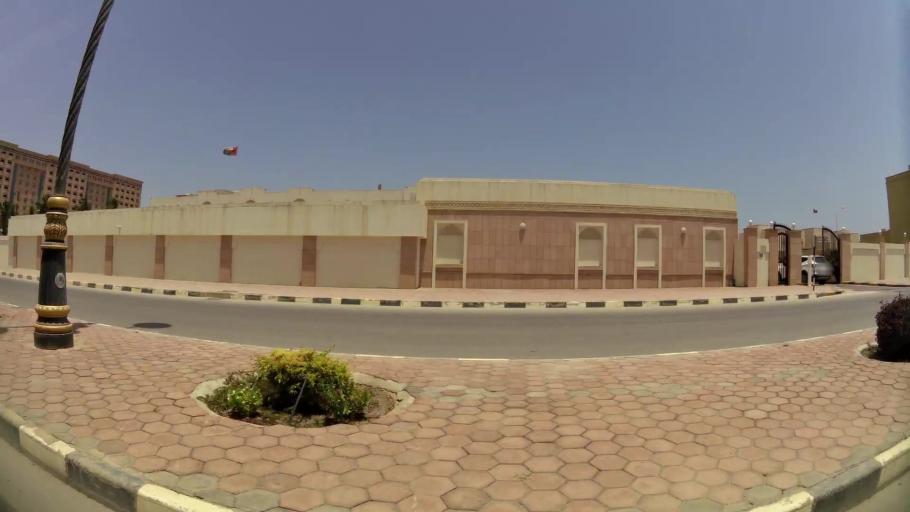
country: OM
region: Zufar
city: Salalah
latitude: 17.0222
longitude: 54.0903
